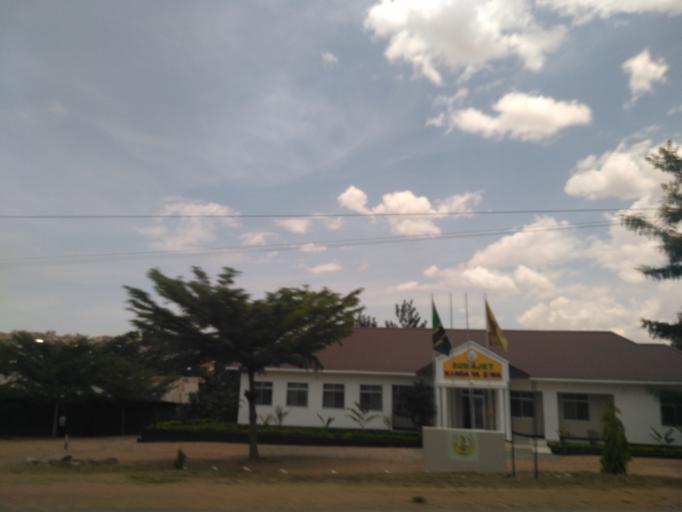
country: TZ
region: Mwanza
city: Mwanza
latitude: -2.5689
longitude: 32.9196
